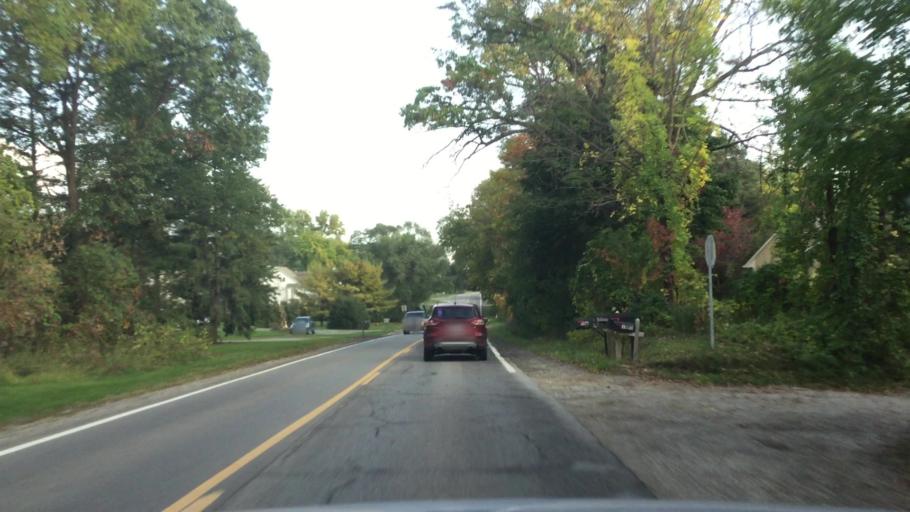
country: US
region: Michigan
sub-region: Oakland County
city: Wolverine Lake
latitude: 42.6214
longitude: -83.4514
